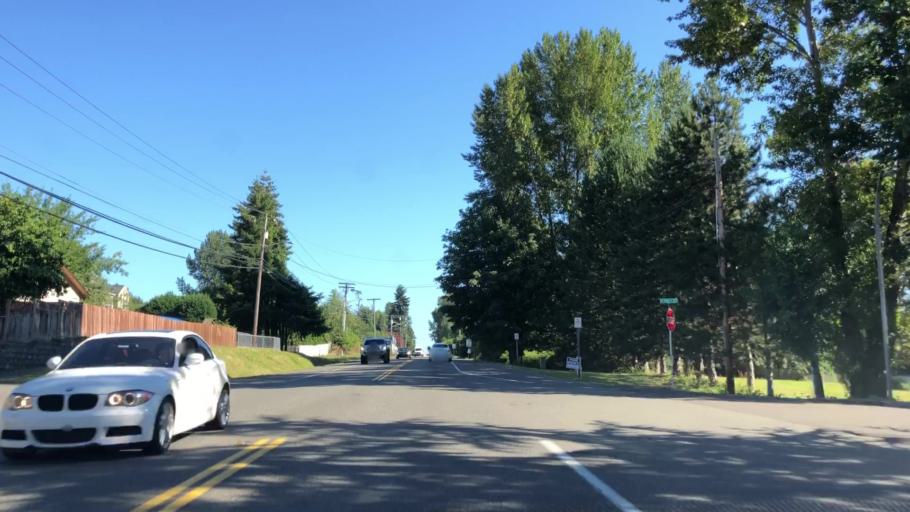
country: US
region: Washington
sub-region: King County
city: Inglewood-Finn Hill
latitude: 47.7260
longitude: -122.2078
